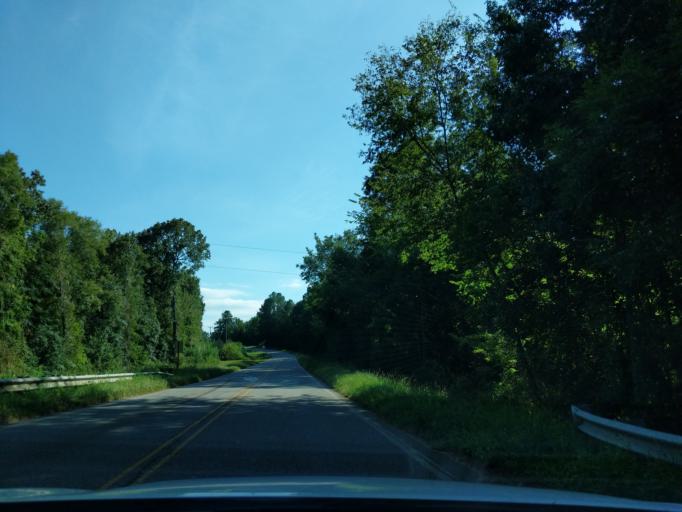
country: US
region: Georgia
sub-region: Oglethorpe County
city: Lexington
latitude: 33.8871
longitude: -82.9919
